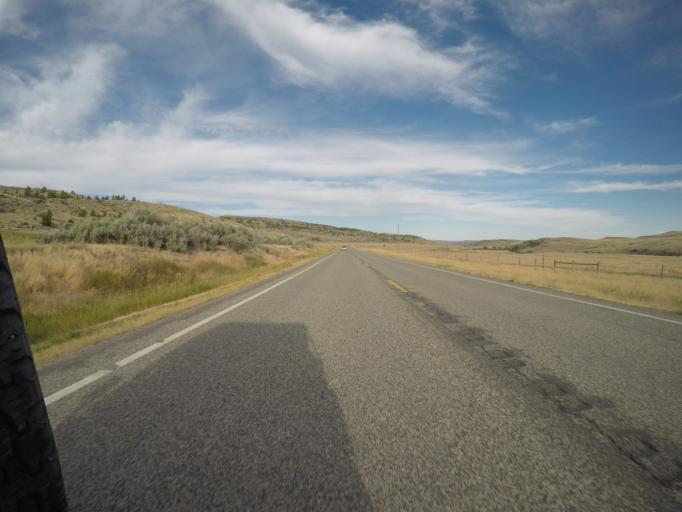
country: US
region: Montana
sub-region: Carbon County
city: Red Lodge
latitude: 45.1653
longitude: -109.1093
